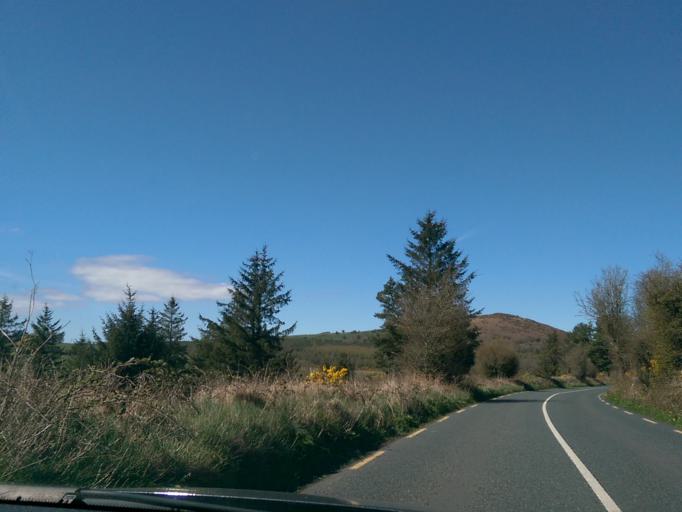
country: IE
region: Leinster
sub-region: Wicklow
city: Carnew
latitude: 52.8409
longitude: -6.5432
